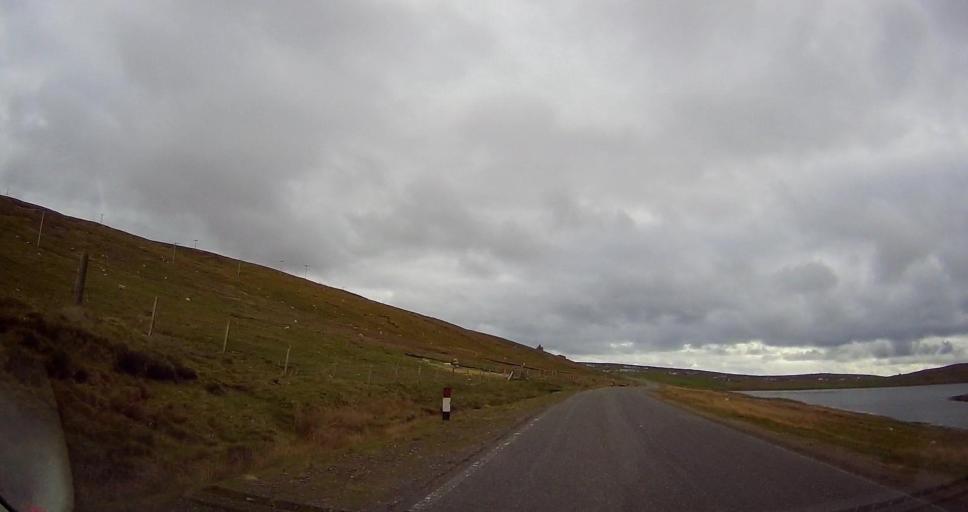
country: GB
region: Scotland
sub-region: Shetland Islands
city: Shetland
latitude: 60.6065
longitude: -1.0871
